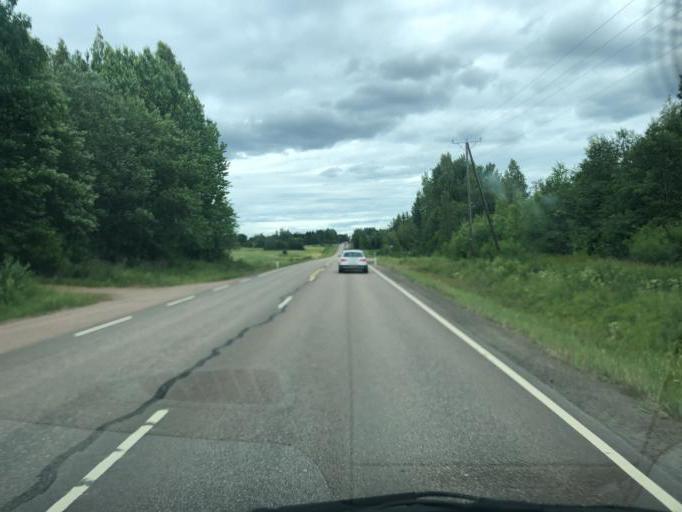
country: FI
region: Southern Savonia
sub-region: Mikkeli
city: Maentyharju
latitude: 61.0814
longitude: 27.0629
